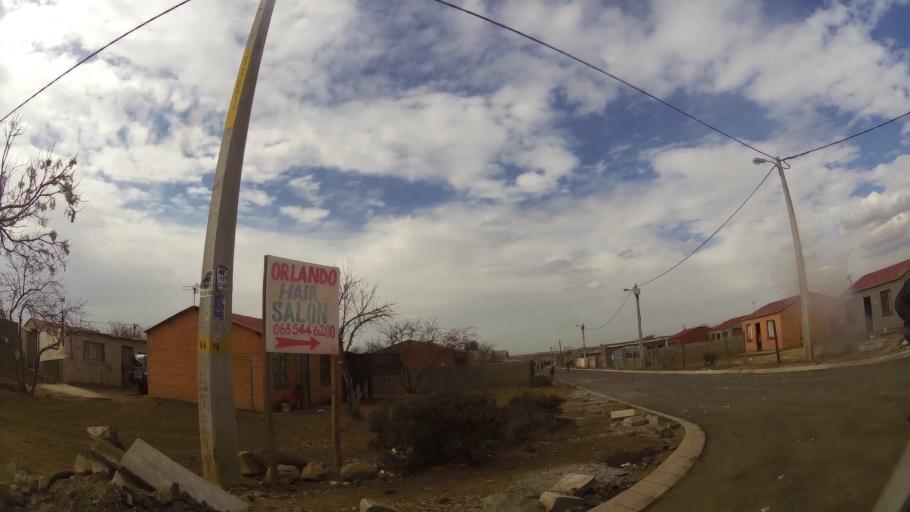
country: ZA
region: Gauteng
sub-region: Ekurhuleni Metropolitan Municipality
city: Germiston
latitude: -26.4052
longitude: 28.1613
